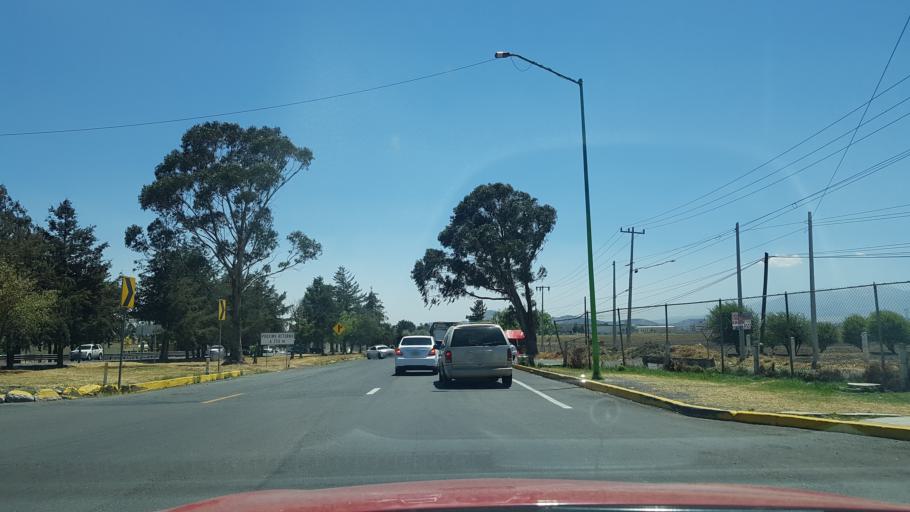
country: MX
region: Mexico
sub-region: Toluca
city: Sebastian Lerdo de Tejada
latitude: 19.4074
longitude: -99.7159
